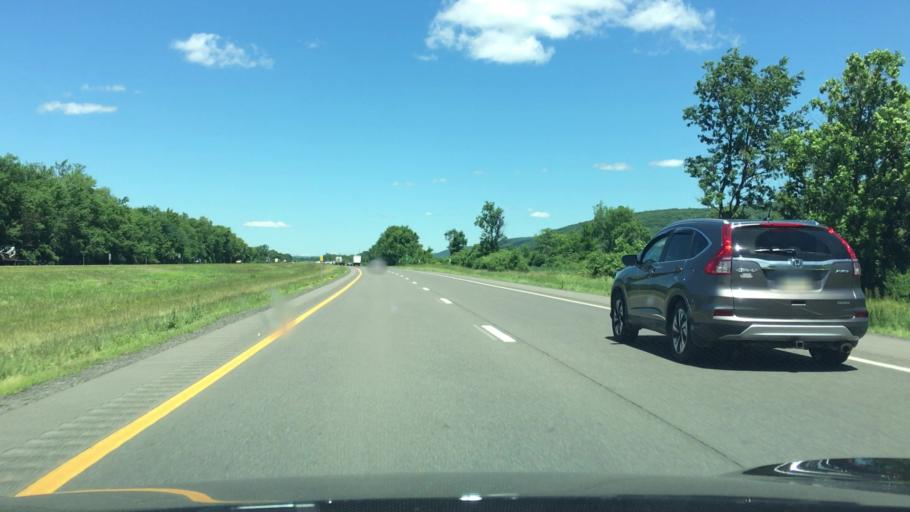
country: US
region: New York
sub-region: Cortland County
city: Homer
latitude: 42.6697
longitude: -76.1690
